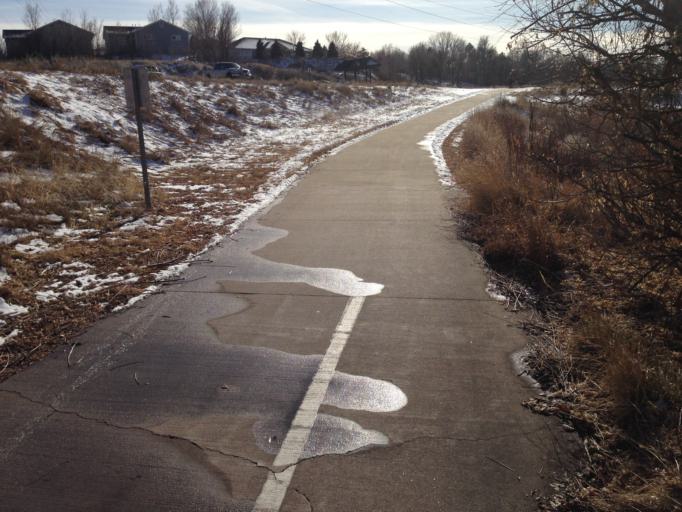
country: US
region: Colorado
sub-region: Adams County
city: Berkley
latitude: 39.7976
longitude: -105.0350
